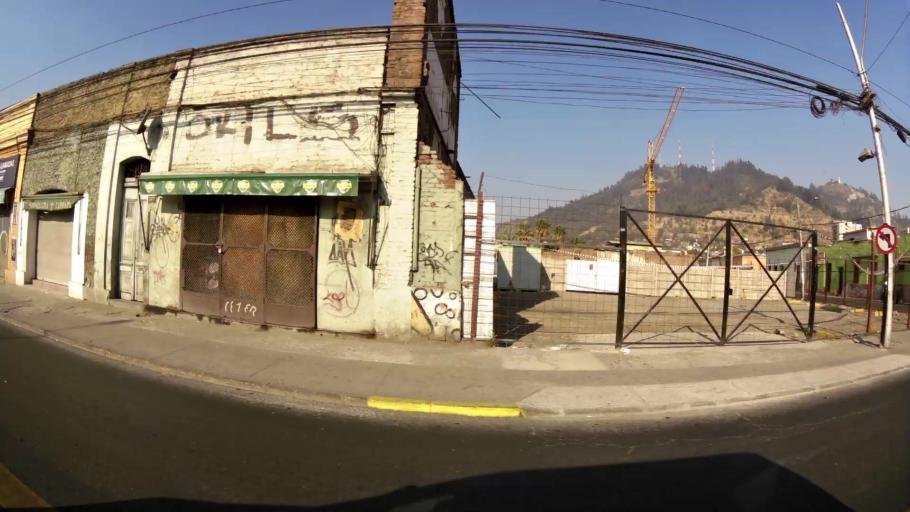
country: CL
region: Santiago Metropolitan
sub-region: Provincia de Santiago
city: Santiago
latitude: -33.4146
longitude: -70.6435
